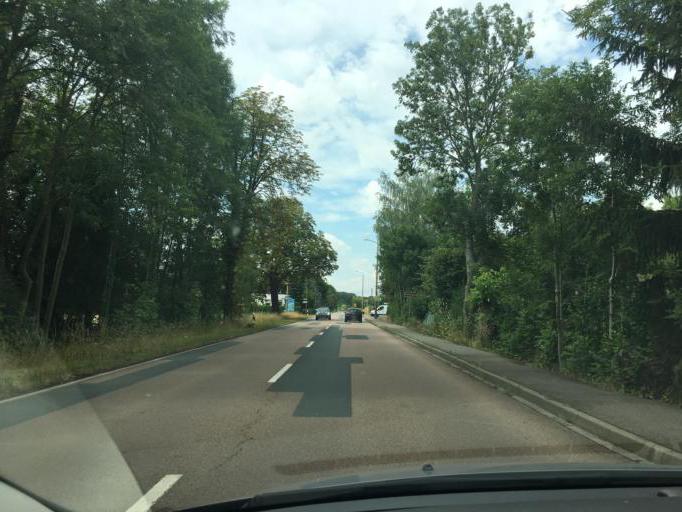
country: DE
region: Saxony-Anhalt
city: Holleben
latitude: 51.4200
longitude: 11.9348
